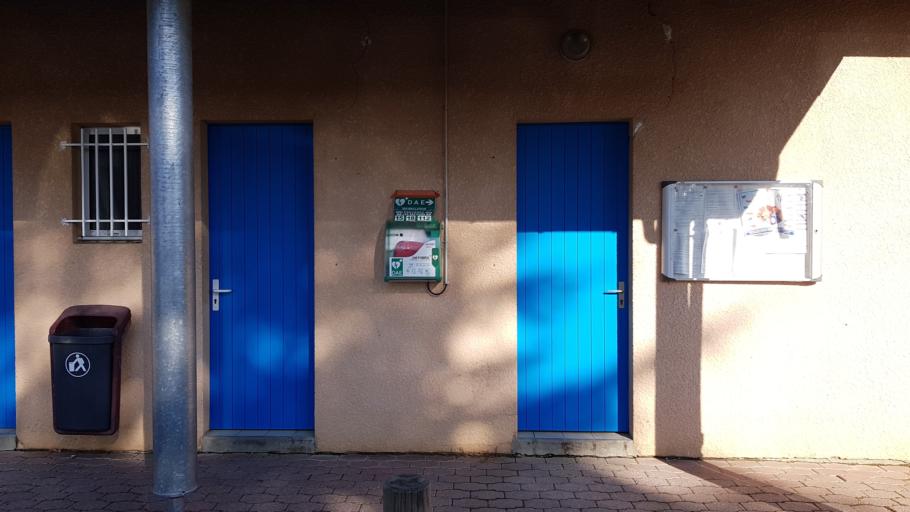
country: FR
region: Aquitaine
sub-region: Departement des Landes
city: Saint-Paul-les-Dax
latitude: 43.7333
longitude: -1.0662
